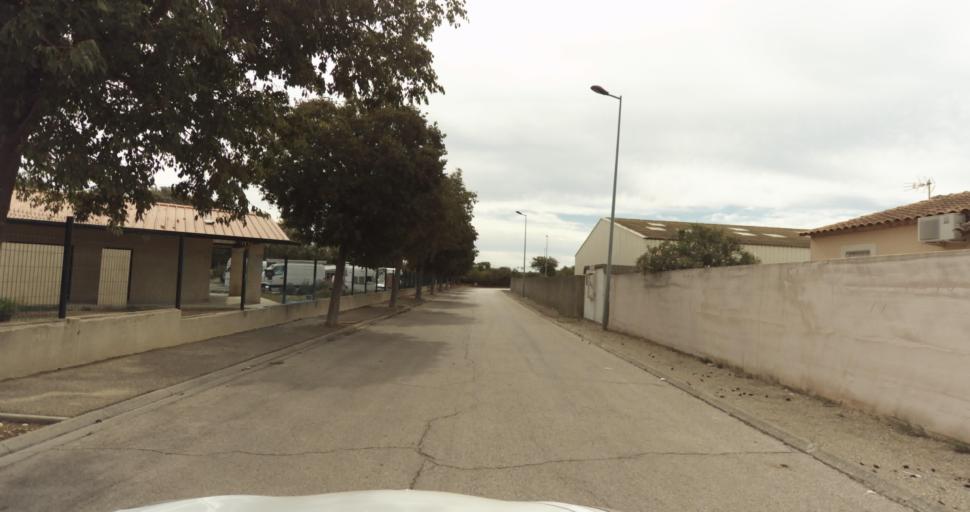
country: FR
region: Provence-Alpes-Cote d'Azur
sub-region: Departement des Bouches-du-Rhone
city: Miramas
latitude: 43.5991
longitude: 4.9972
